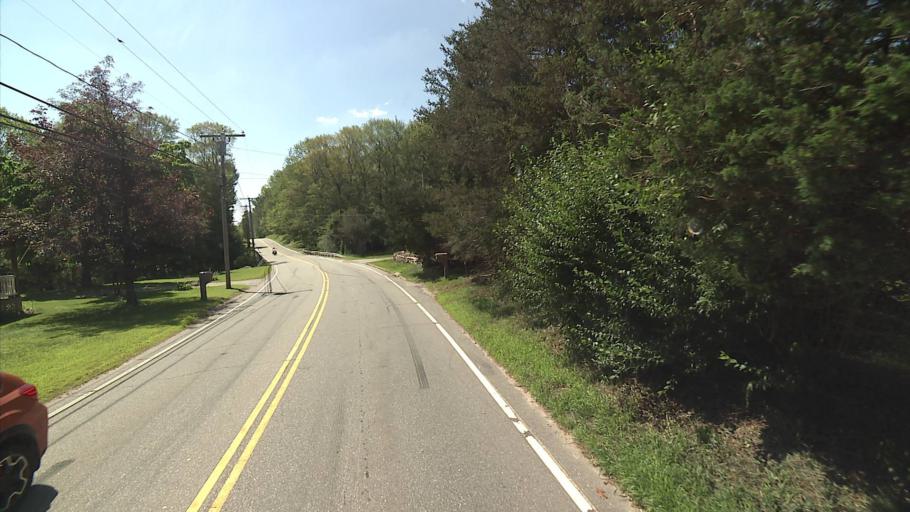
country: US
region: Connecticut
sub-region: Windham County
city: Moosup
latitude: 41.7127
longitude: -71.8447
